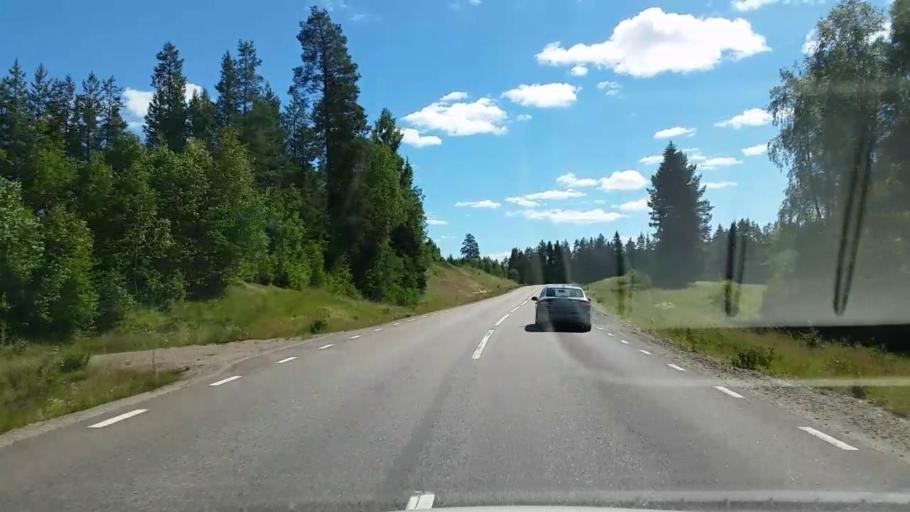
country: SE
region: Gaevleborg
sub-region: Ovanakers Kommun
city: Edsbyn
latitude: 61.1899
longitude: 15.8760
